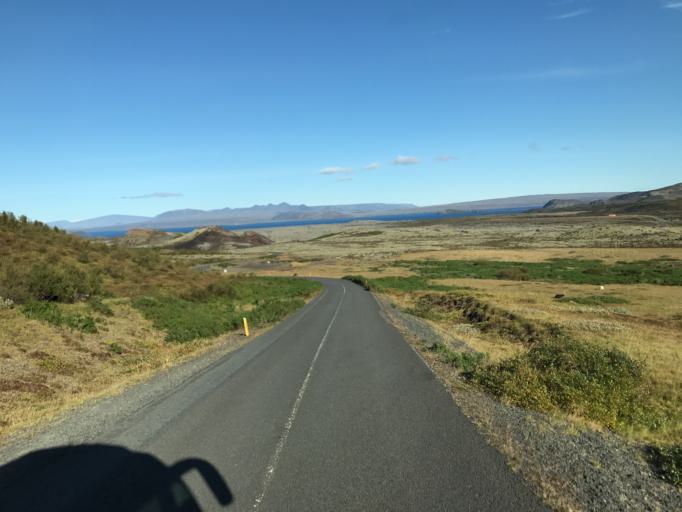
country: IS
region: South
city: Hveragerdi
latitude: 64.1198
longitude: -21.2606
